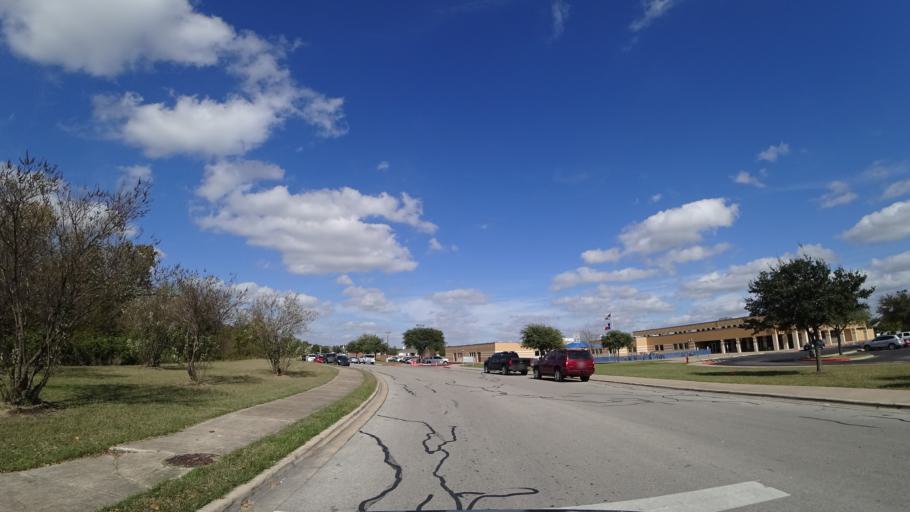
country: US
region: Texas
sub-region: Travis County
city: Windemere
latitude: 30.4679
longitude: -97.6562
